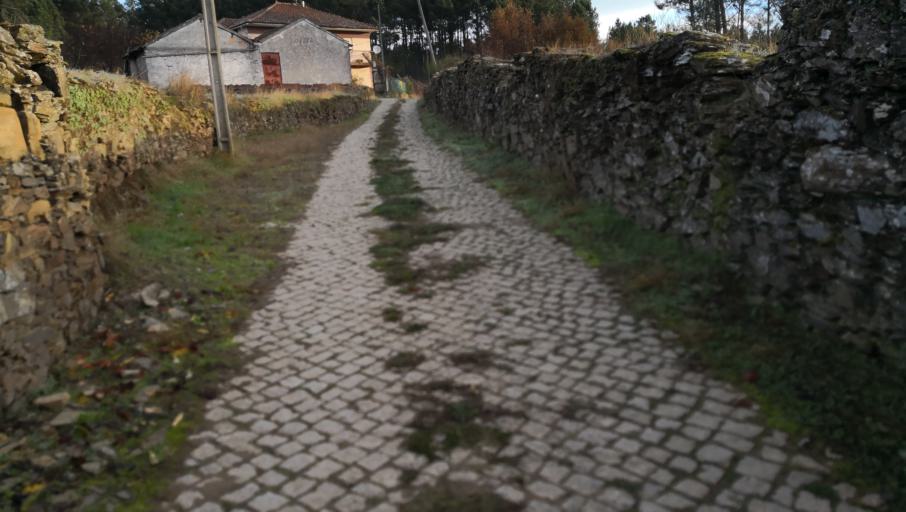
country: PT
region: Vila Real
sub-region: Sabrosa
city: Vilela
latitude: 41.2525
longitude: -7.6342
